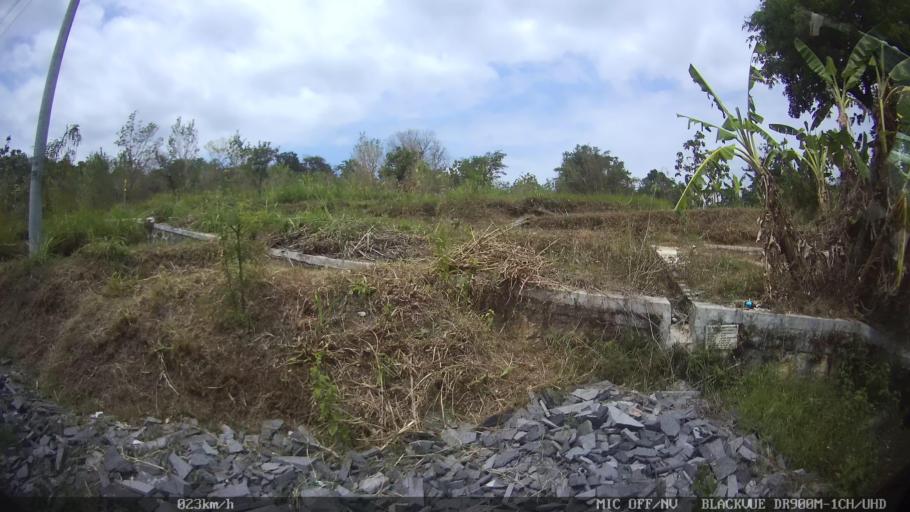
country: ID
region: Central Java
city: Candi Prambanan
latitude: -7.7840
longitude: 110.4987
